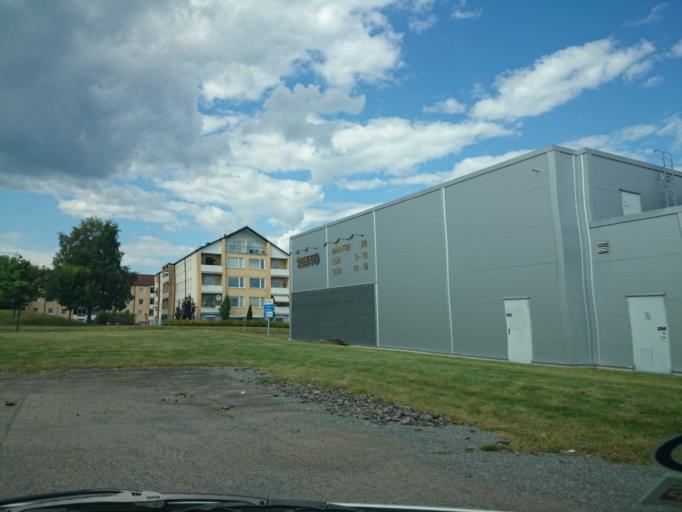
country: SE
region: Joenkoeping
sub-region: Varnamo Kommun
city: Varnamo
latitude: 57.1829
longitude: 14.0300
